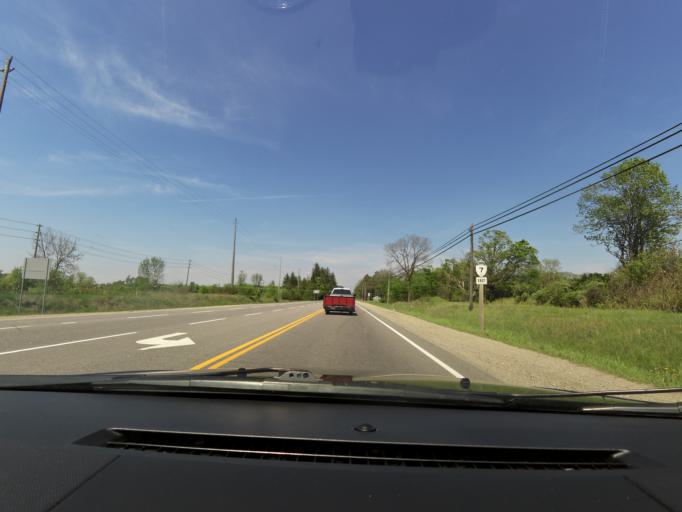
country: CA
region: Ontario
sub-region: Wellington County
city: Guelph
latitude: 43.5907
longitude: -80.1774
